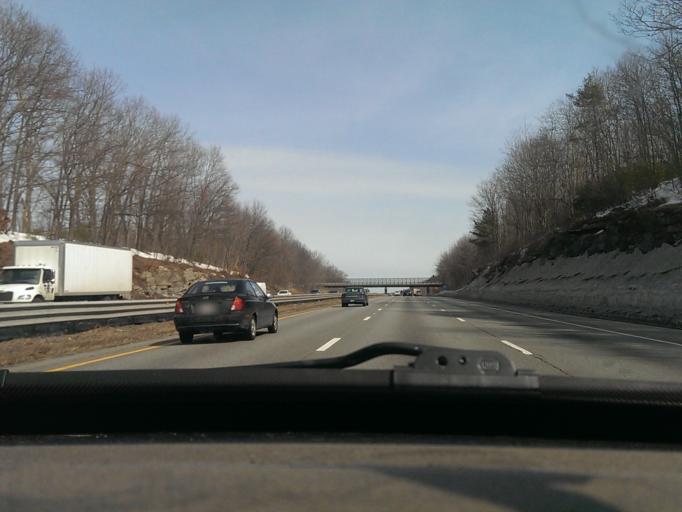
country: US
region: Massachusetts
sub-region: Worcester County
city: Auburn
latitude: 42.1827
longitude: -71.8924
